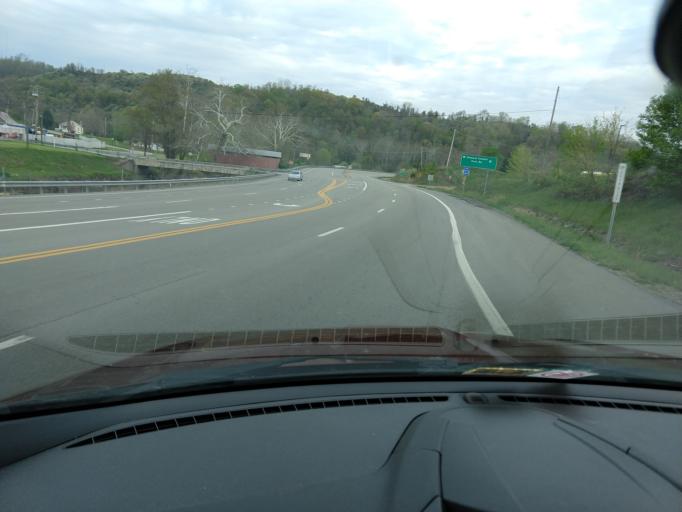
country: US
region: West Virginia
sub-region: Harrison County
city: Bridgeport
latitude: 39.3093
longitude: -80.2773
